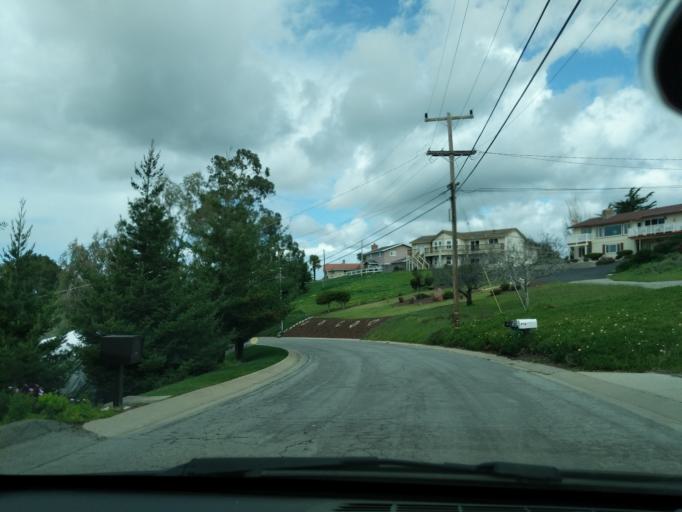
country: US
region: California
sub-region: Monterey County
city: Prunedale
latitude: 36.7618
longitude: -121.6614
